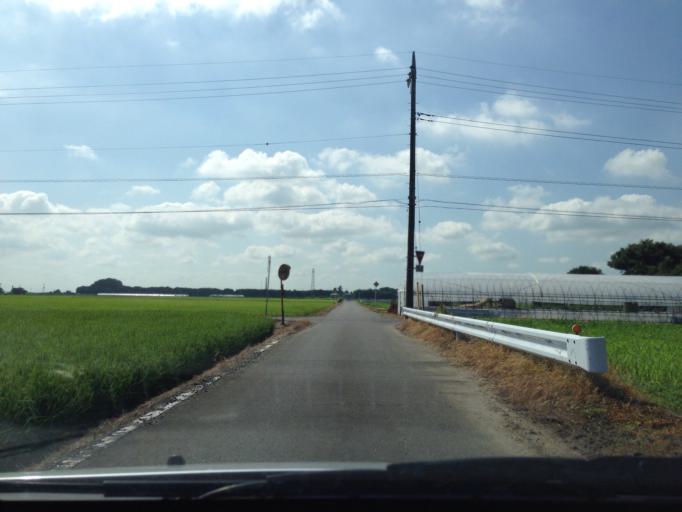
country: JP
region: Ibaraki
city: Inashiki
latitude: 36.0119
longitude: 140.3649
